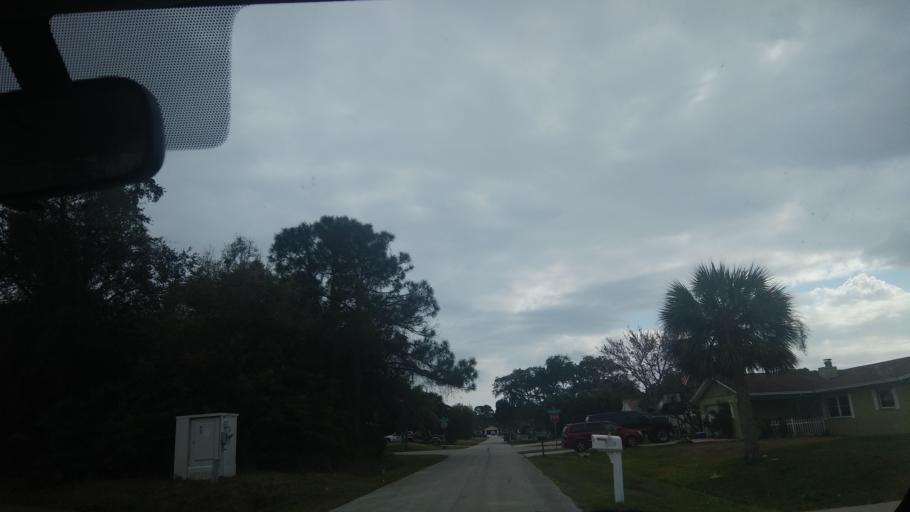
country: US
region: Florida
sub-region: Indian River County
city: Sebastian
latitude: 27.8036
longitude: -80.4903
